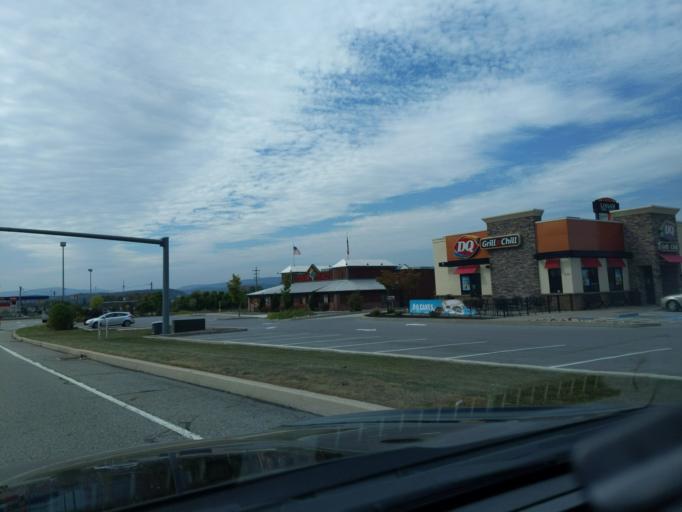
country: US
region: Pennsylvania
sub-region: Blair County
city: Lakemont
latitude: 40.4873
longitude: -78.3870
